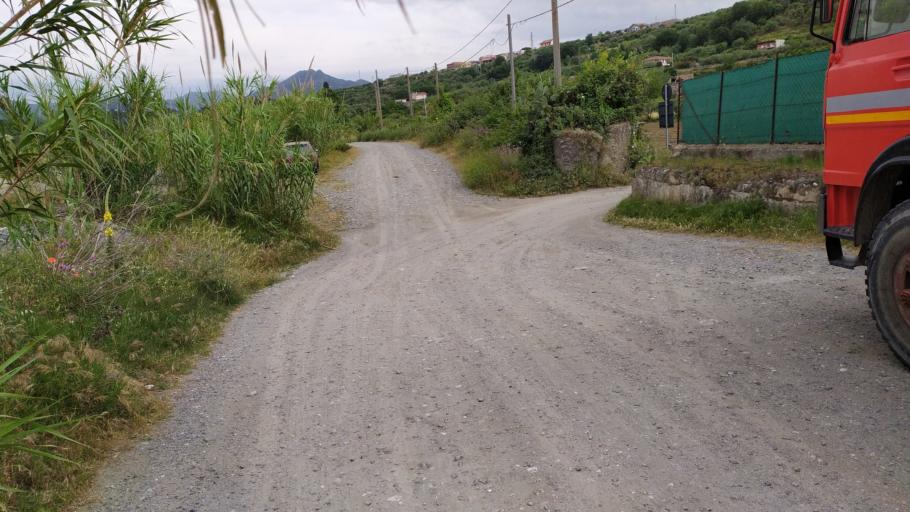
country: IT
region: Sicily
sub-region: Messina
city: San Filippo del Mela
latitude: 38.1802
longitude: 15.2733
